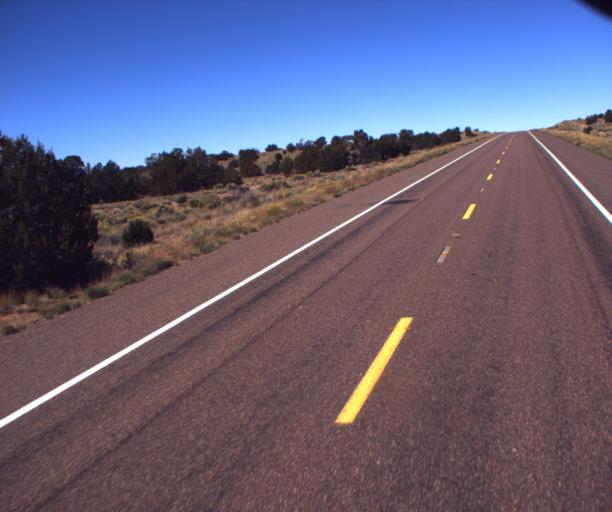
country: US
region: Arizona
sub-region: Apache County
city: Saint Johns
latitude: 34.6527
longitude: -109.7076
